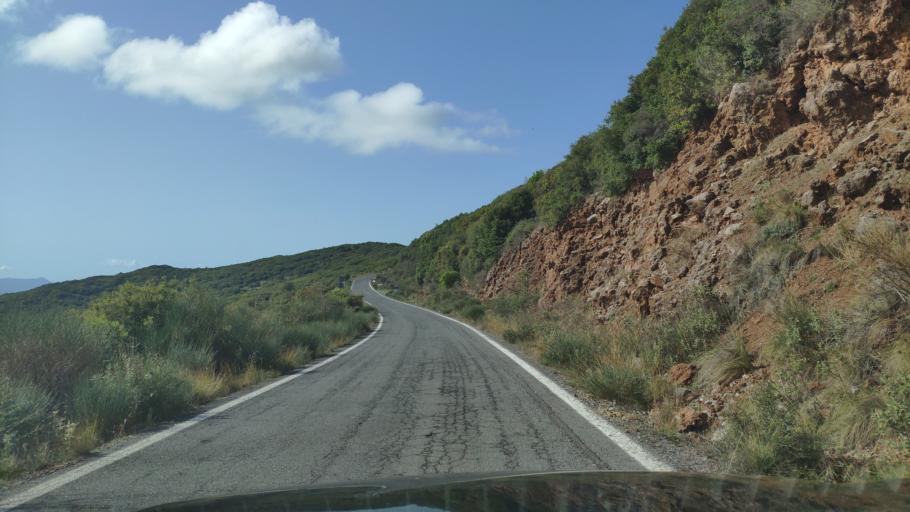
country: GR
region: Peloponnese
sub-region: Nomos Arkadias
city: Dimitsana
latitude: 37.5728
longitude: 22.0068
